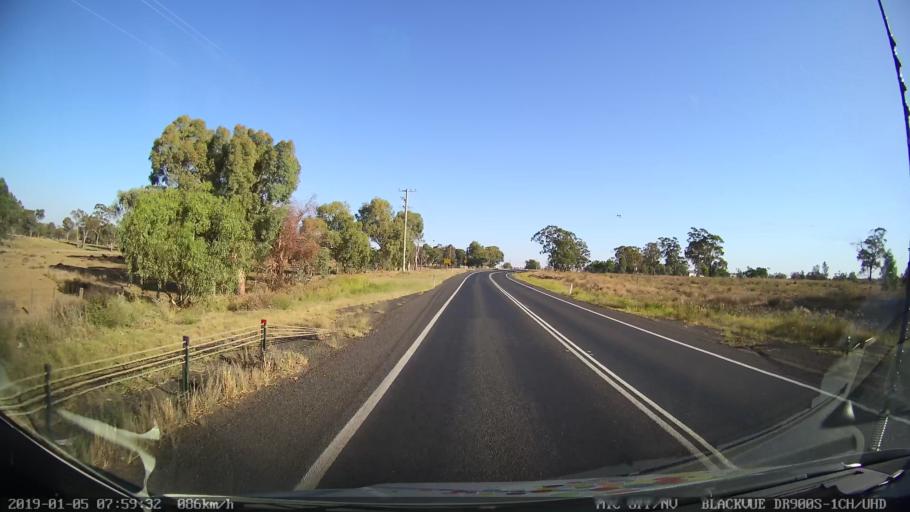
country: AU
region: New South Wales
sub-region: Gilgandra
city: Gilgandra
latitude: -31.7010
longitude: 148.6792
